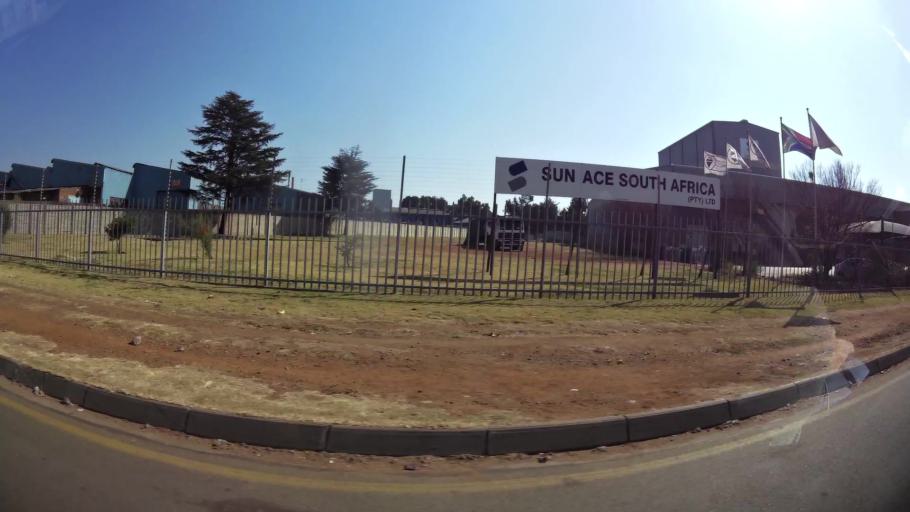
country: ZA
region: Gauteng
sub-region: Ekurhuleni Metropolitan Municipality
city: Boksburg
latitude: -26.1663
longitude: 28.2099
